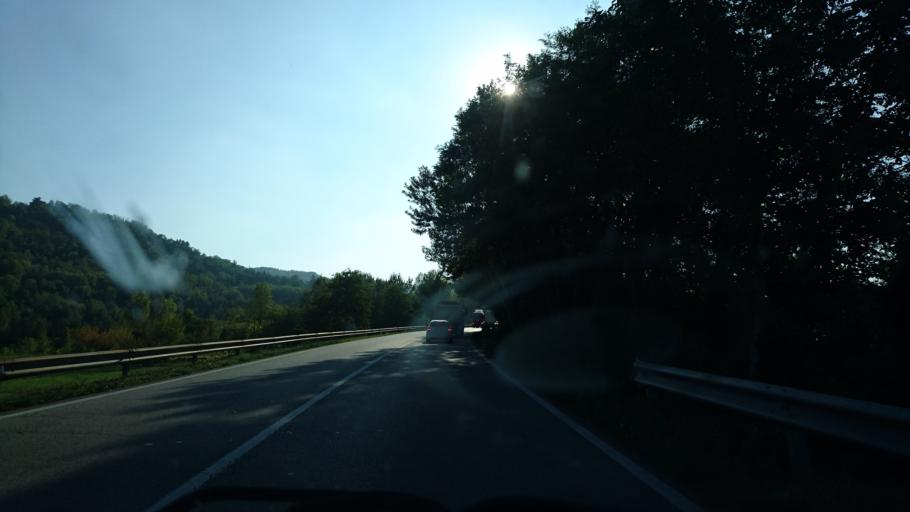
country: IT
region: Piedmont
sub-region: Provincia di Alessandria
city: Acqui Terme
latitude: 44.6679
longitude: 8.4797
